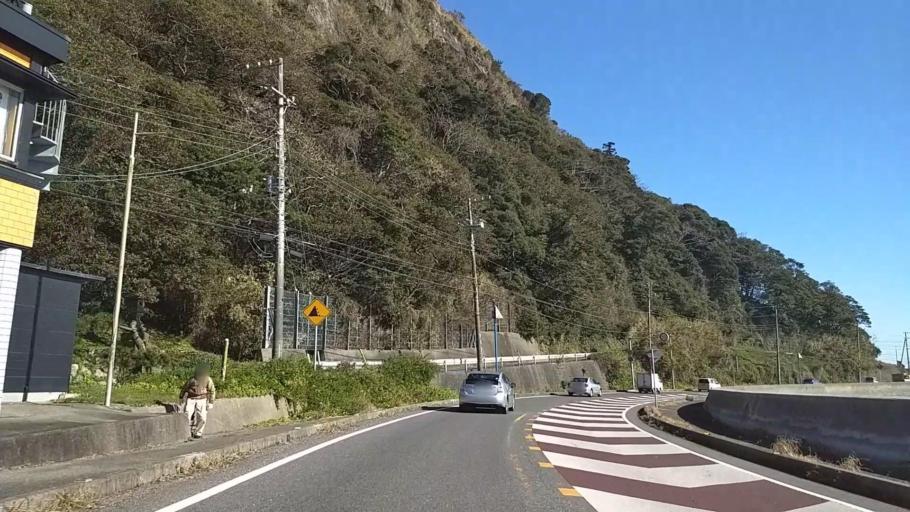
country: JP
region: Chiba
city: Kawaguchi
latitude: 35.0743
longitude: 140.0852
